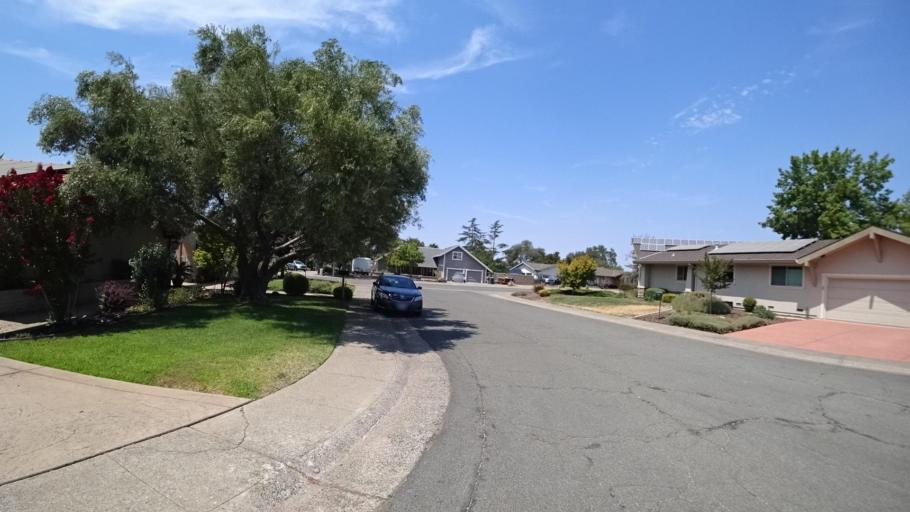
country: US
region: California
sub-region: Placer County
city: Rocklin
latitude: 38.8004
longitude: -121.2450
